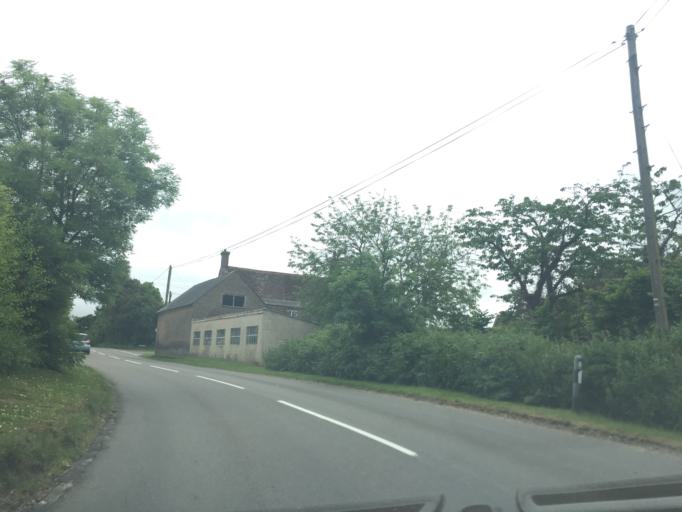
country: GB
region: England
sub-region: Dorset
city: Wareham
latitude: 50.6730
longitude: -2.1618
